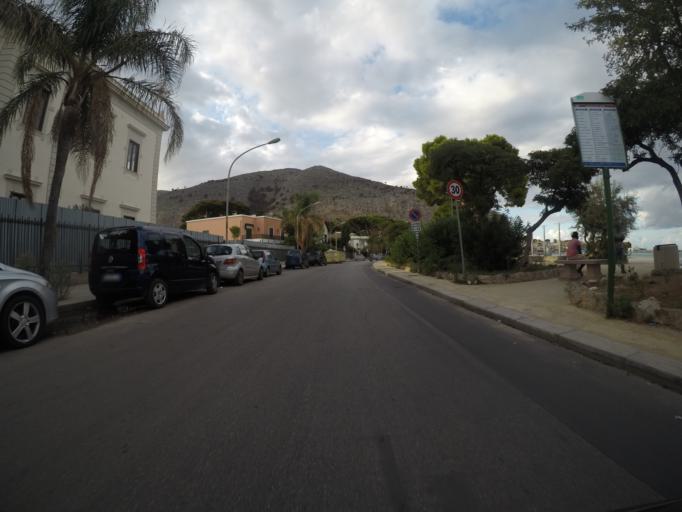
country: IT
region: Sicily
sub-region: Palermo
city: Palermo
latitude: 38.2036
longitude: 13.3255
